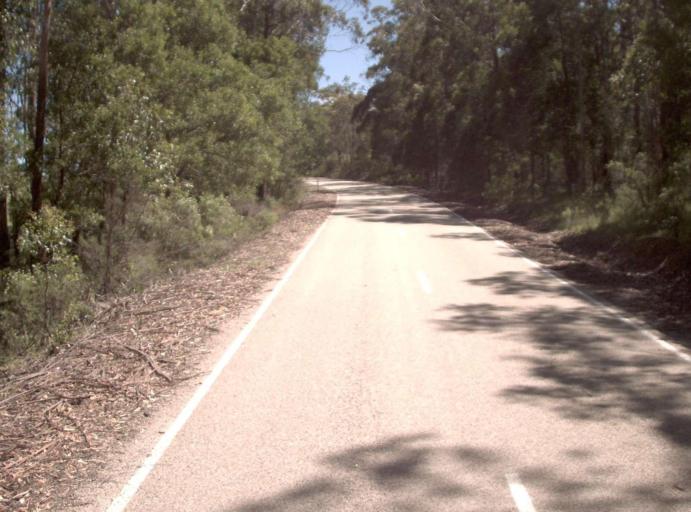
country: AU
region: Victoria
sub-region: East Gippsland
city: Lakes Entrance
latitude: -37.3055
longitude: 148.2468
